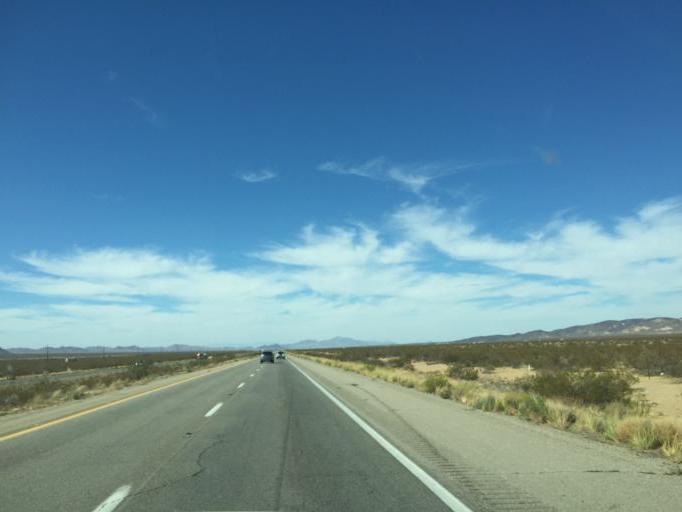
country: US
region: Arizona
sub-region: Mohave County
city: Dolan Springs
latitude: 35.5699
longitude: -114.3800
